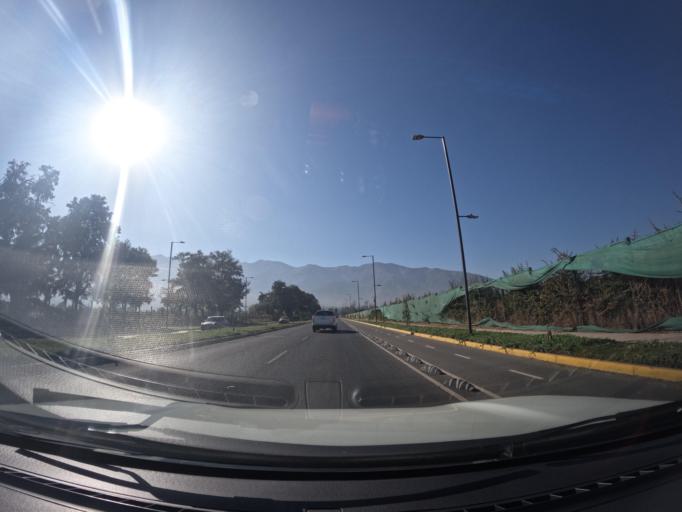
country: CL
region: Santiago Metropolitan
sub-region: Provincia de Santiago
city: Villa Presidente Frei, Nunoa, Santiago, Chile
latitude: -33.4901
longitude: -70.5635
